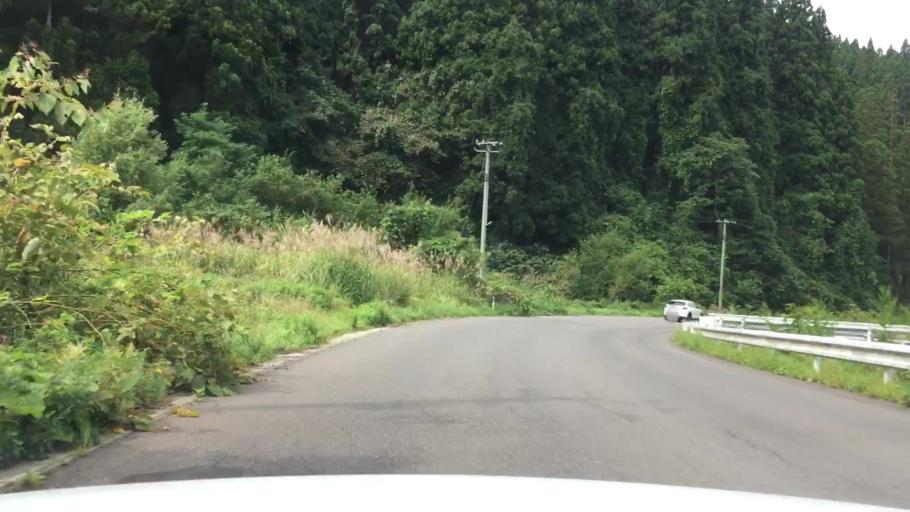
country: JP
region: Aomori
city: Shimokizukuri
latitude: 40.7385
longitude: 140.2461
